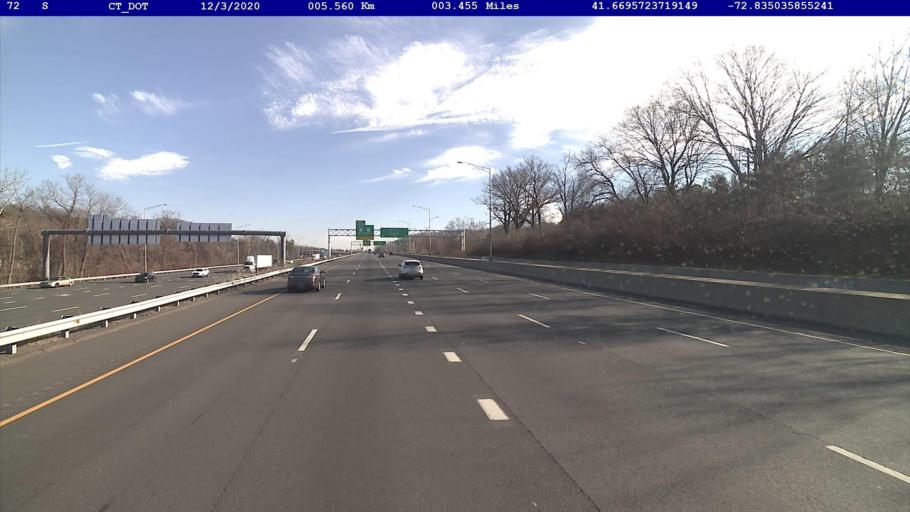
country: US
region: Connecticut
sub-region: Hartford County
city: Plainville
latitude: 41.6660
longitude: -72.8366
